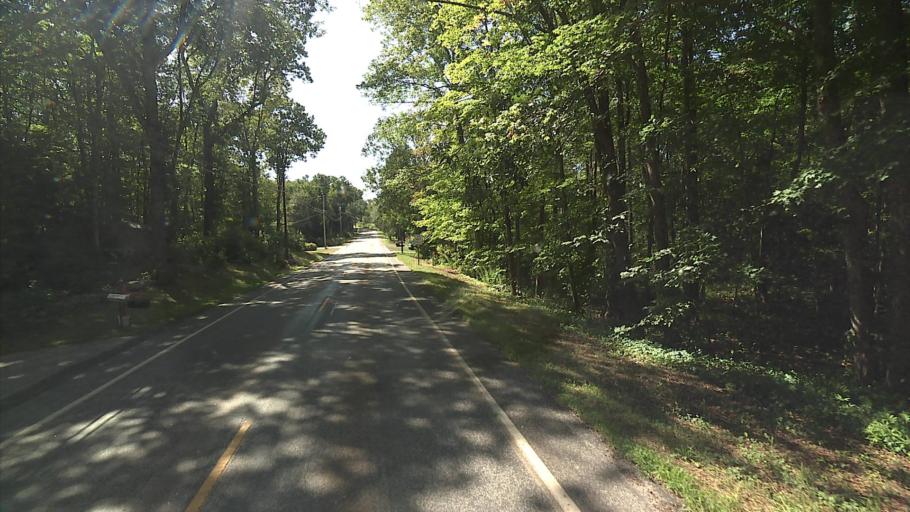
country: US
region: Connecticut
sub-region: Litchfield County
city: Thomaston
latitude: 41.7204
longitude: -73.0708
